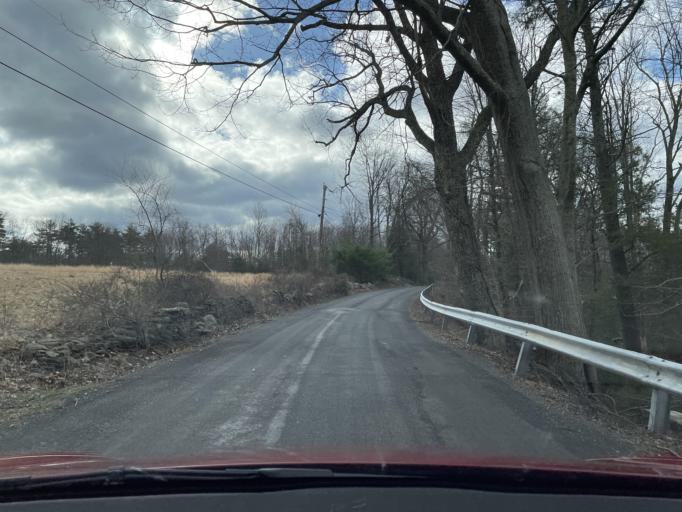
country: US
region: New York
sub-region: Ulster County
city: Woodstock
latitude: 42.0482
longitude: -74.1563
